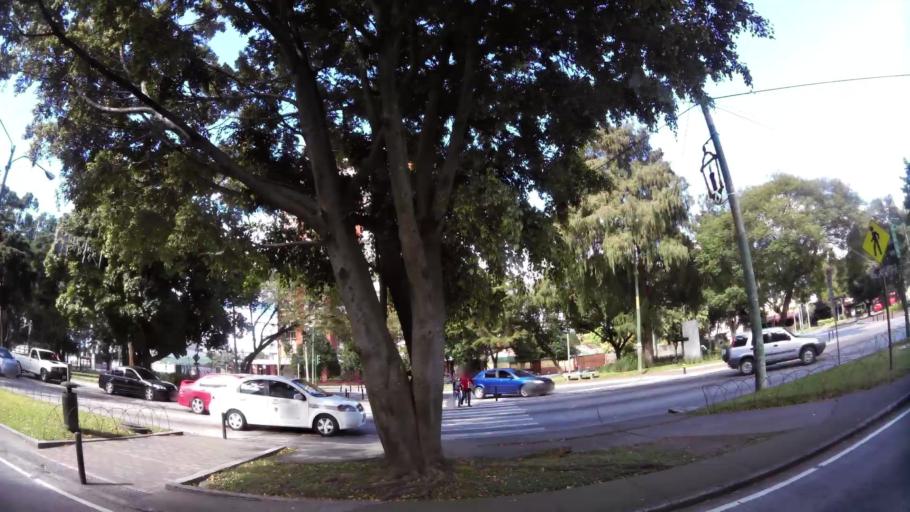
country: GT
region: Guatemala
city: Santa Catarina Pinula
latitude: 14.5982
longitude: -90.5168
